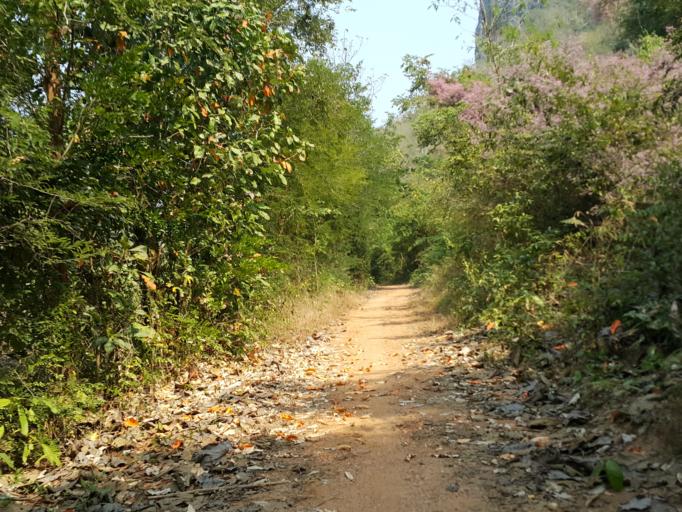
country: TH
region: Sukhothai
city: Thung Saliam
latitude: 17.3027
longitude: 99.5030
